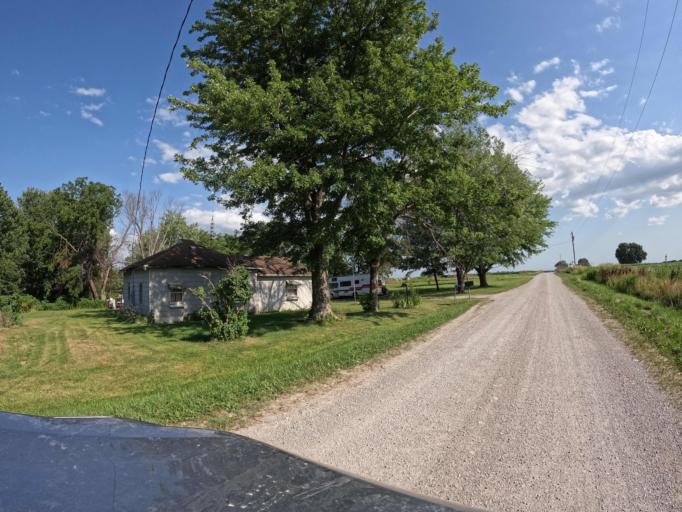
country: US
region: Iowa
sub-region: Appanoose County
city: Centerville
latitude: 40.7174
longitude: -93.0304
